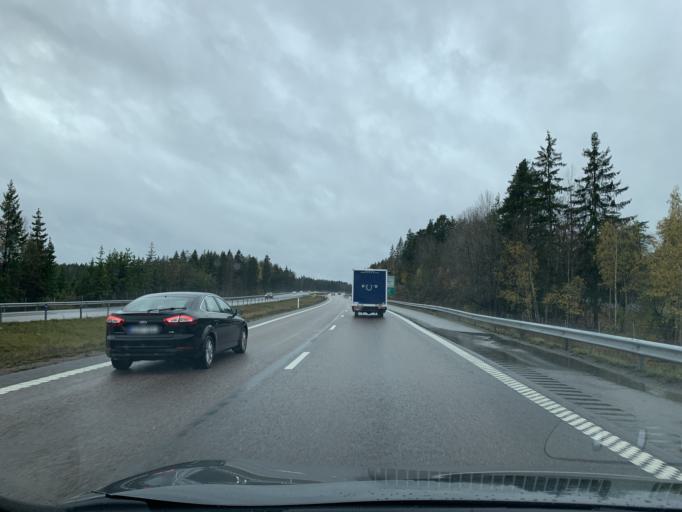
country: SE
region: Soedermanland
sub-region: Trosa Kommun
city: Vagnharad
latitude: 58.9284
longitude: 17.3976
